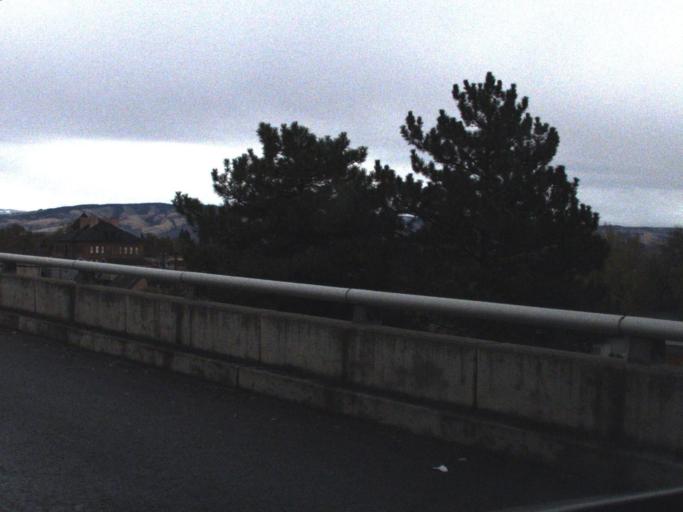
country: US
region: Washington
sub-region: Walla Walla County
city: Walla Walla
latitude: 46.0696
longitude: -118.3553
